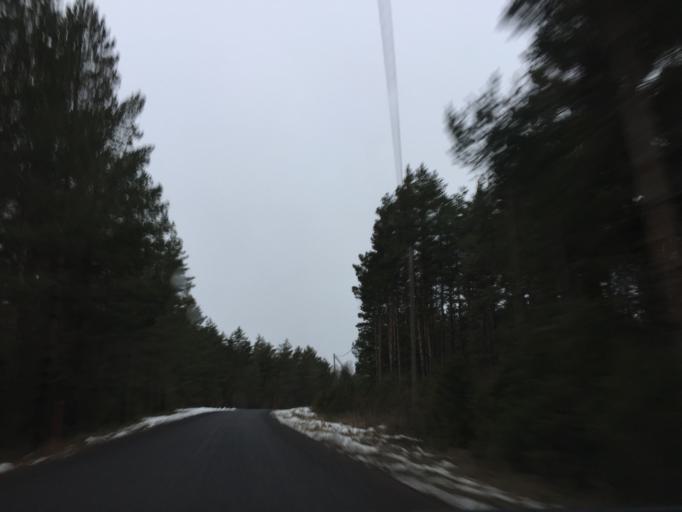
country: EE
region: Laeaene
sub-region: Lihula vald
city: Lihula
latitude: 58.6588
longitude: 23.5841
